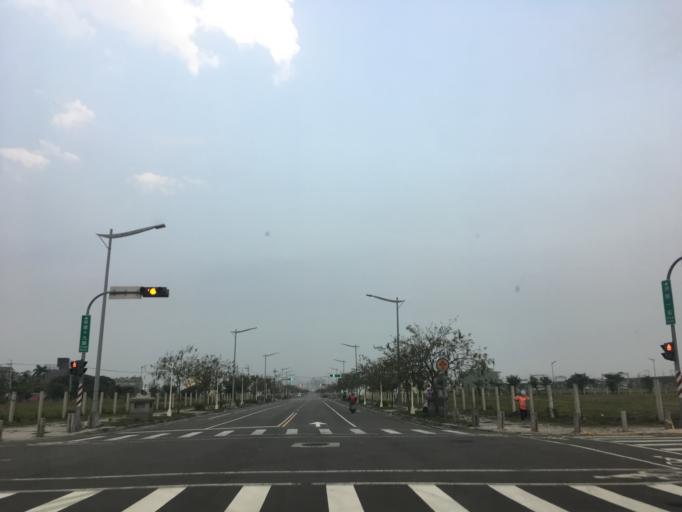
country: TW
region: Taiwan
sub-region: Taichung City
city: Taichung
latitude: 24.1979
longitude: 120.6820
